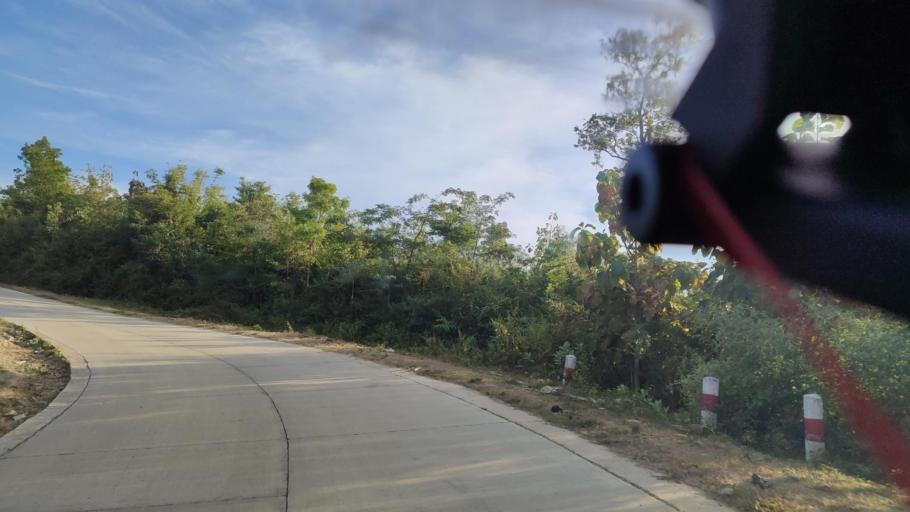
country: MM
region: Magway
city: Taungdwingyi
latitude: 20.0216
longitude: 95.7926
